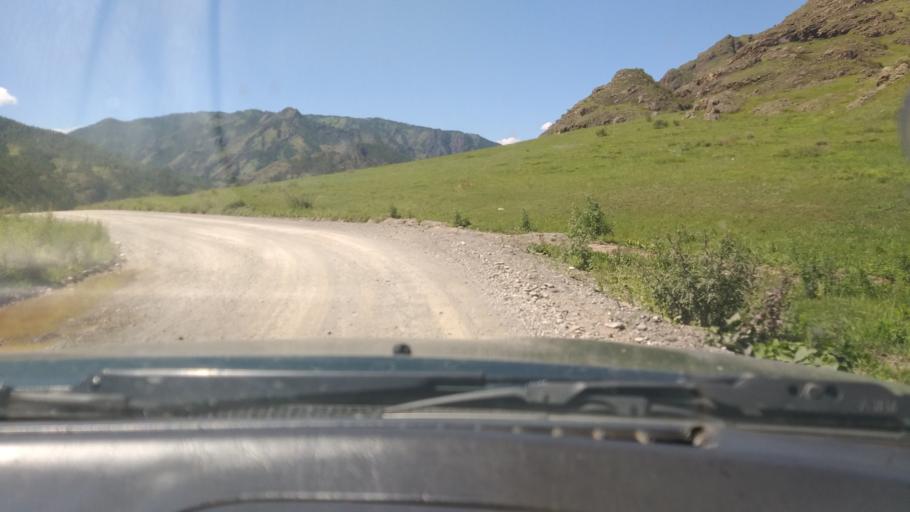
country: RU
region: Altay
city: Chemal
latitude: 51.1636
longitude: 86.1429
